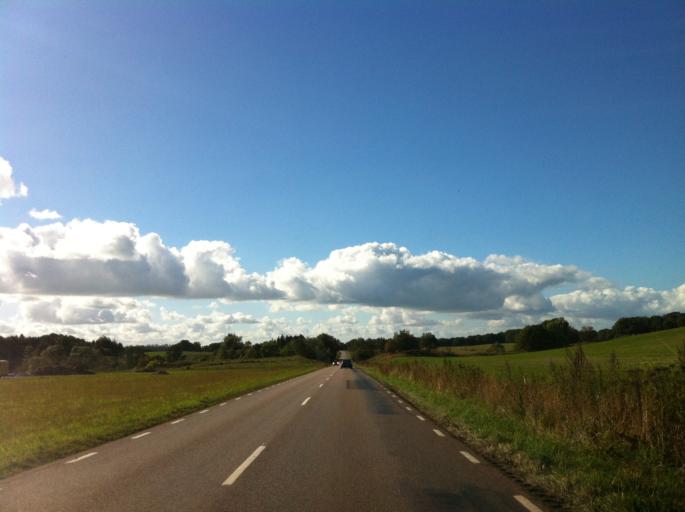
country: SE
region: Skane
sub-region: Sjobo Kommun
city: Sjoebo
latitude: 55.6390
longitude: 13.7709
